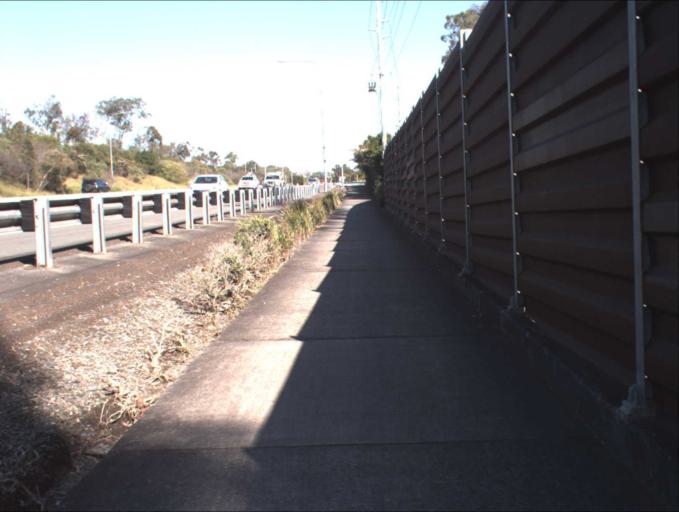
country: AU
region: Queensland
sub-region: Logan
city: Beenleigh
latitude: -27.7120
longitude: 153.1750
